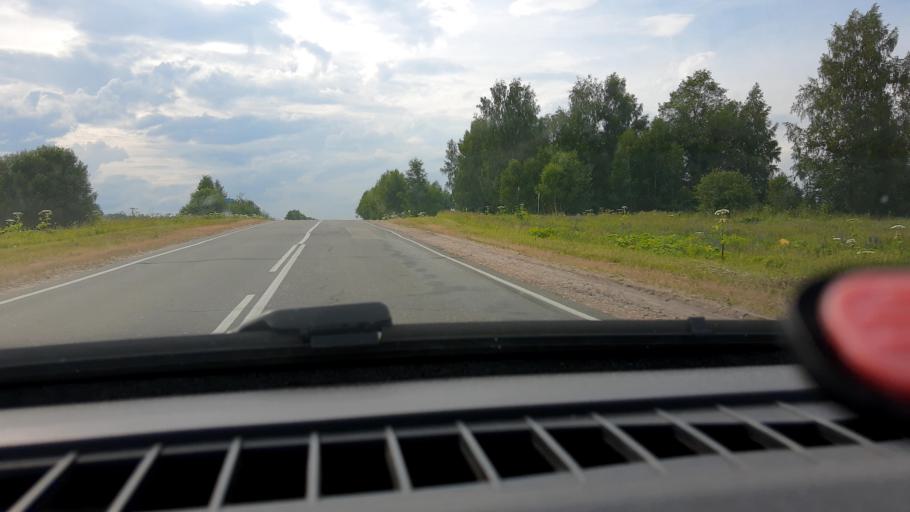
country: RU
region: Nizjnij Novgorod
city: Sitniki
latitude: 56.4975
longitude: 44.0006
